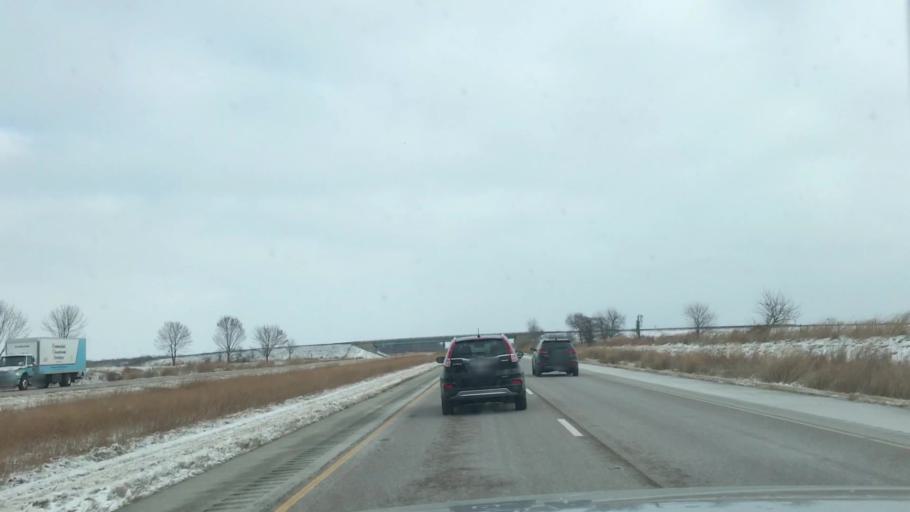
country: US
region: Illinois
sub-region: Macoupin County
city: Mount Olive
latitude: 39.1179
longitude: -89.7216
